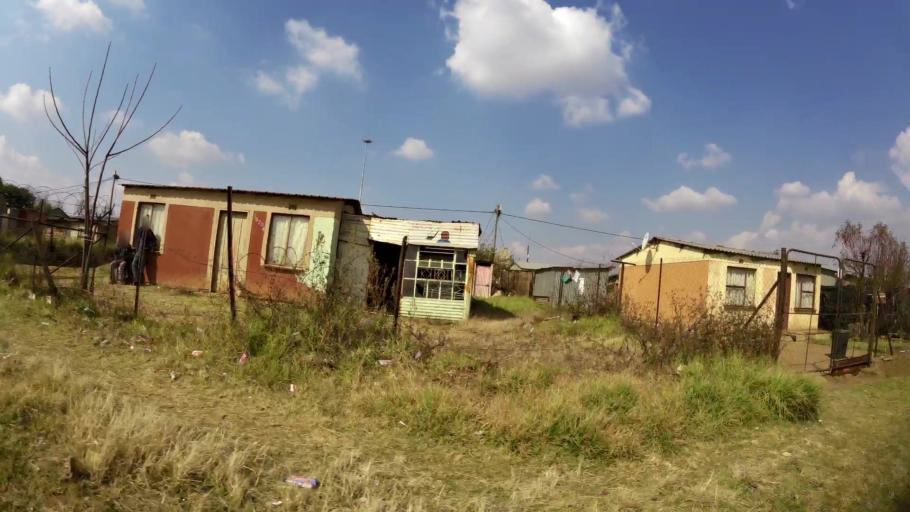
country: ZA
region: Gauteng
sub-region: Ekurhuleni Metropolitan Municipality
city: Springs
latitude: -26.1286
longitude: 28.4833
